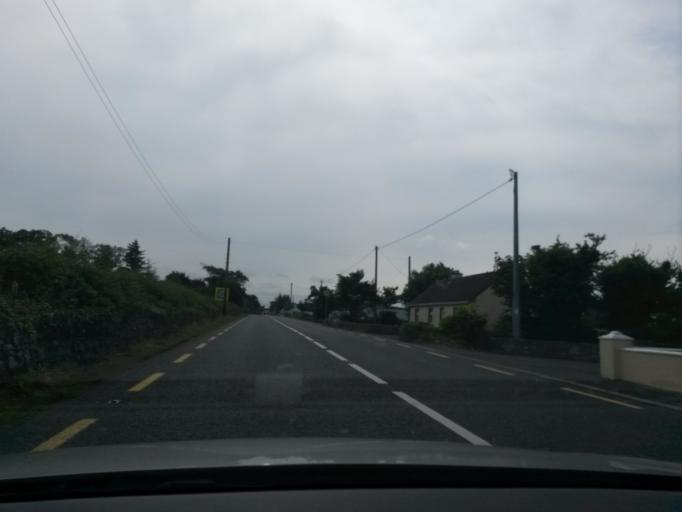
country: IE
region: Connaught
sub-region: Sligo
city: Sligo
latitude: 54.4284
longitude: -8.4583
